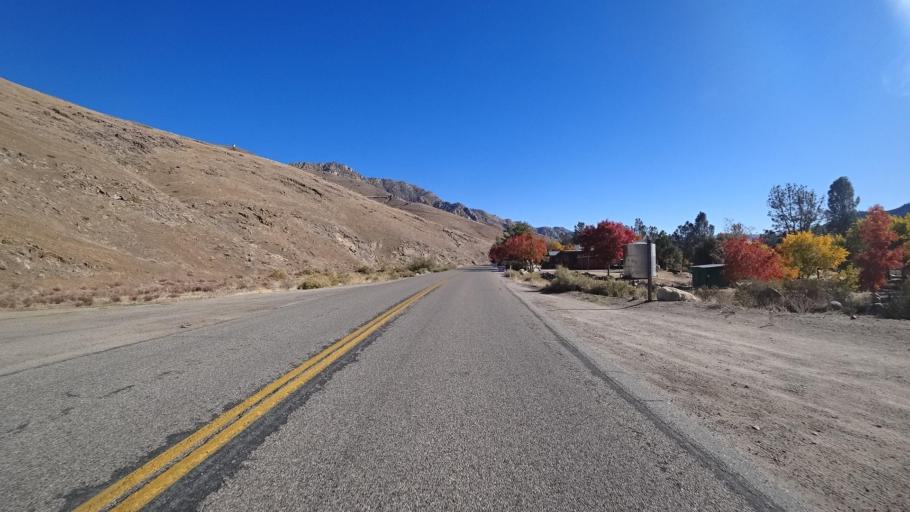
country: US
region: California
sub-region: Kern County
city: Kernville
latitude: 35.7840
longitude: -118.4443
